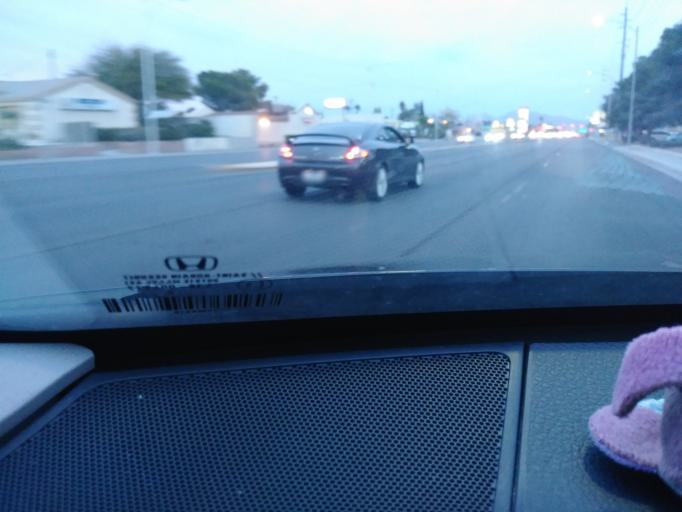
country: US
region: Nevada
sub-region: Clark County
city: Spring Valley
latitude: 36.1591
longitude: -115.2282
